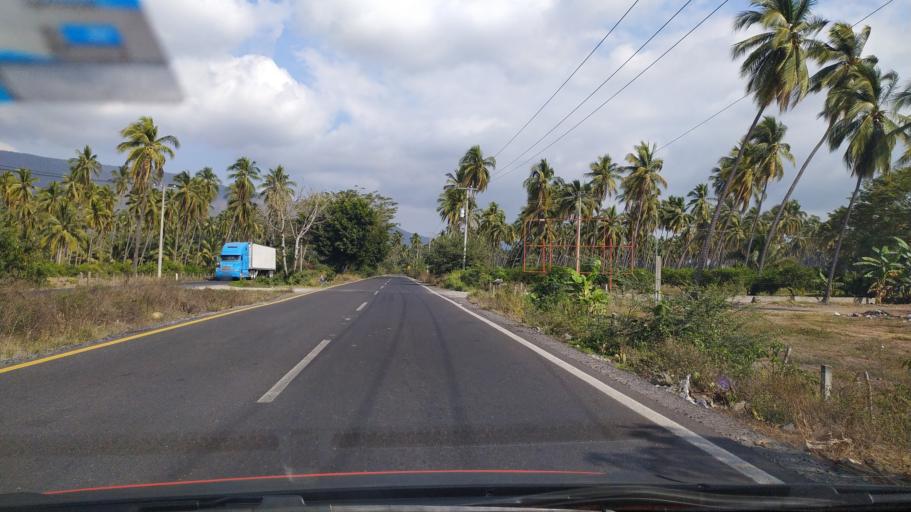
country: MX
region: Colima
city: Tecoman
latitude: 18.9329
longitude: -103.8634
